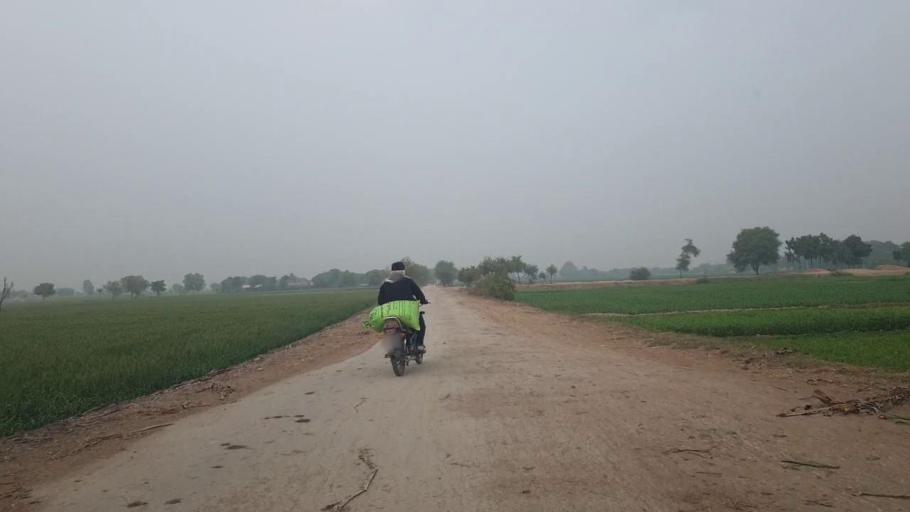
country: PK
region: Sindh
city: Tando Adam
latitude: 25.7649
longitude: 68.7025
